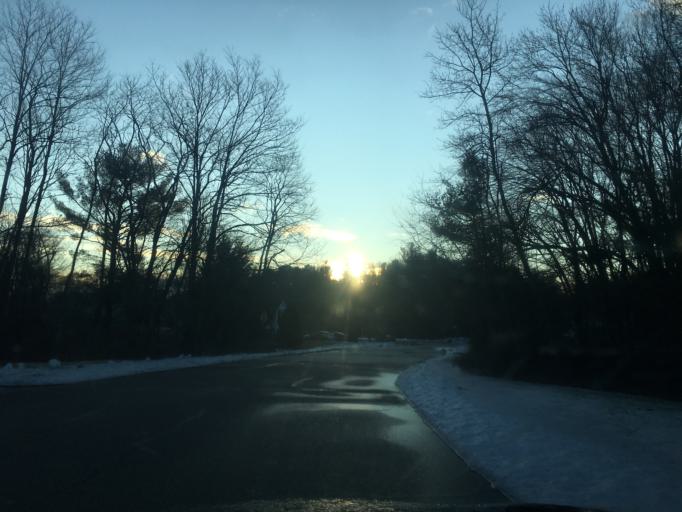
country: US
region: Massachusetts
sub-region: Middlesex County
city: Pinehurst
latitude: 42.5463
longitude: -71.2418
